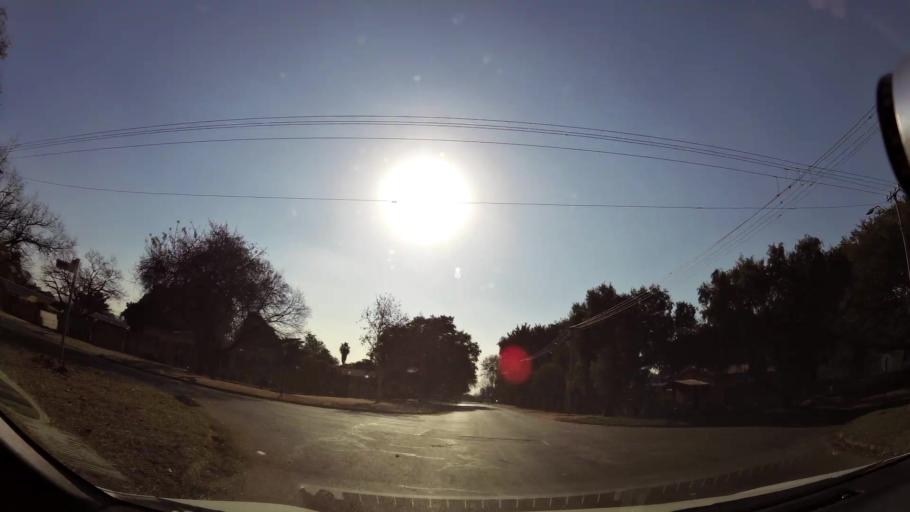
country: ZA
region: North-West
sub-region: Bojanala Platinum District Municipality
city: Rustenburg
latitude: -25.6529
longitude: 27.2540
